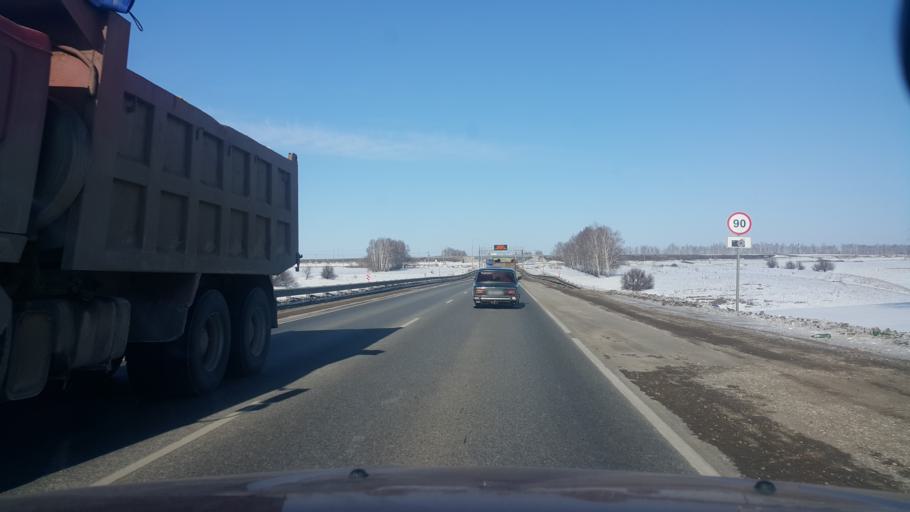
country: RU
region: Tambov
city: Pokrovo-Prigorodnoye
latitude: 52.6552
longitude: 41.3405
